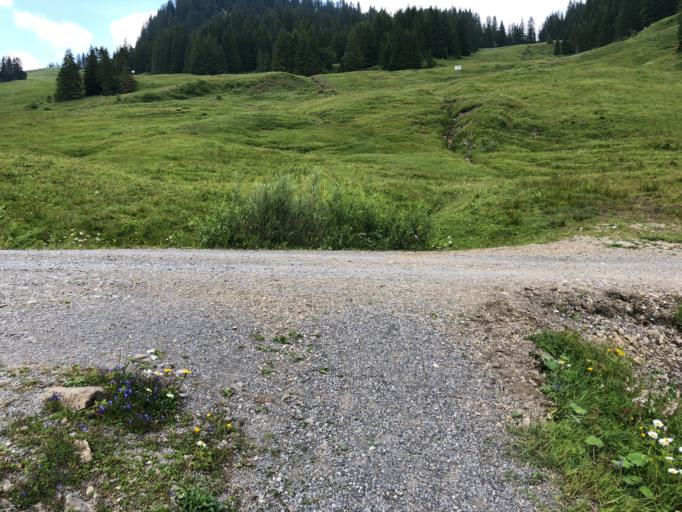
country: AT
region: Vorarlberg
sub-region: Politischer Bezirk Bregenz
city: Reuthe
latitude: 47.3263
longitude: 9.8807
